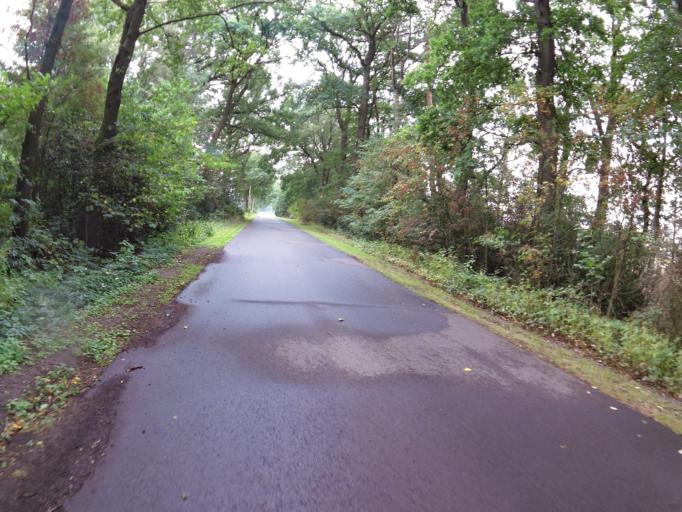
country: DE
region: Lower Saxony
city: Helvesiek
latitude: 53.2165
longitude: 9.4583
